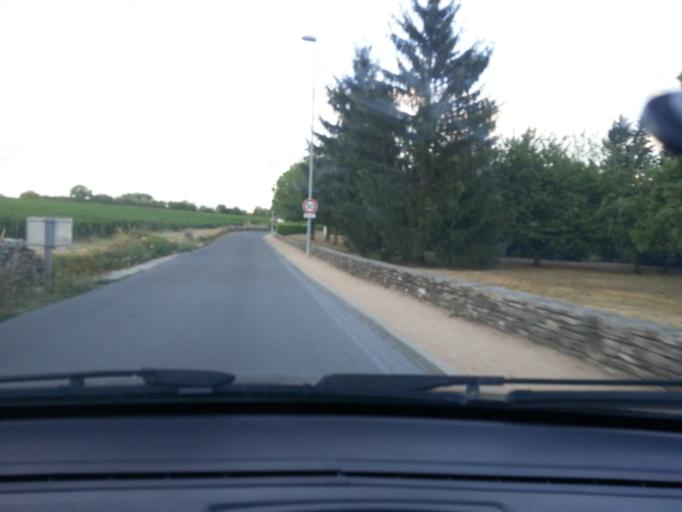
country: FR
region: Bourgogne
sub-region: Departement de Saone-et-Loire
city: Givry
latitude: 46.7798
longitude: 4.7315
